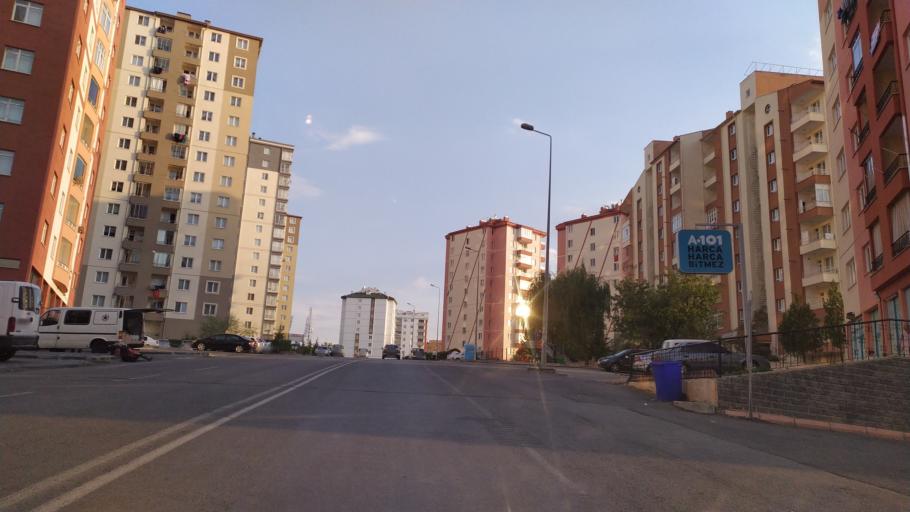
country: TR
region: Kayseri
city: Talas
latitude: 38.7016
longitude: 35.5633
